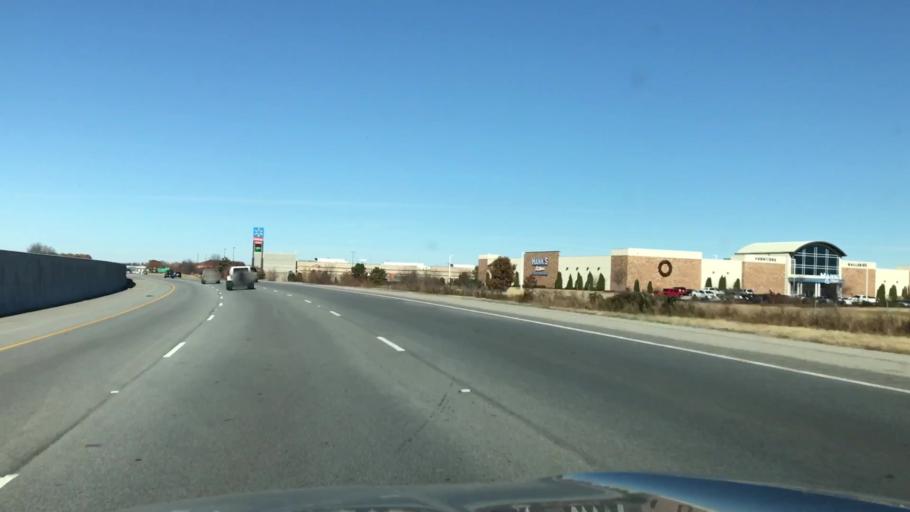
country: US
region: Arkansas
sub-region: Benton County
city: Lowell
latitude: 36.2752
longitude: -94.1505
